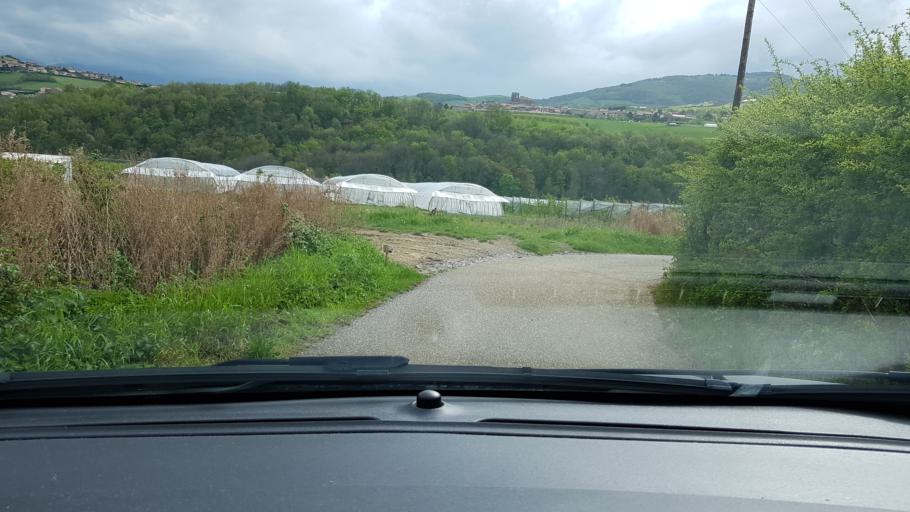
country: FR
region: Rhone-Alpes
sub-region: Departement du Rhone
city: Saint-Didier-sous-Riverie
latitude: 45.6038
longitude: 4.6213
